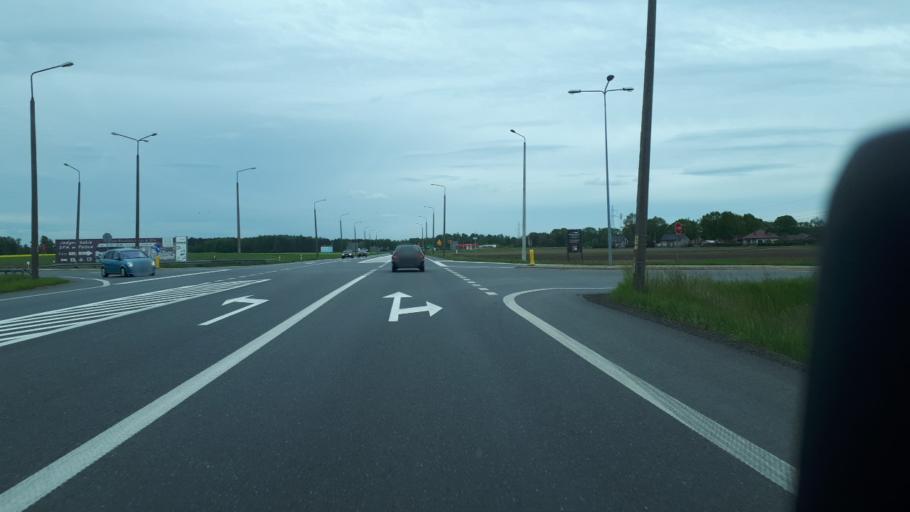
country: PL
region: Opole Voivodeship
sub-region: Powiat kluczborski
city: Kluczbork
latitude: 50.9752
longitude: 18.2565
